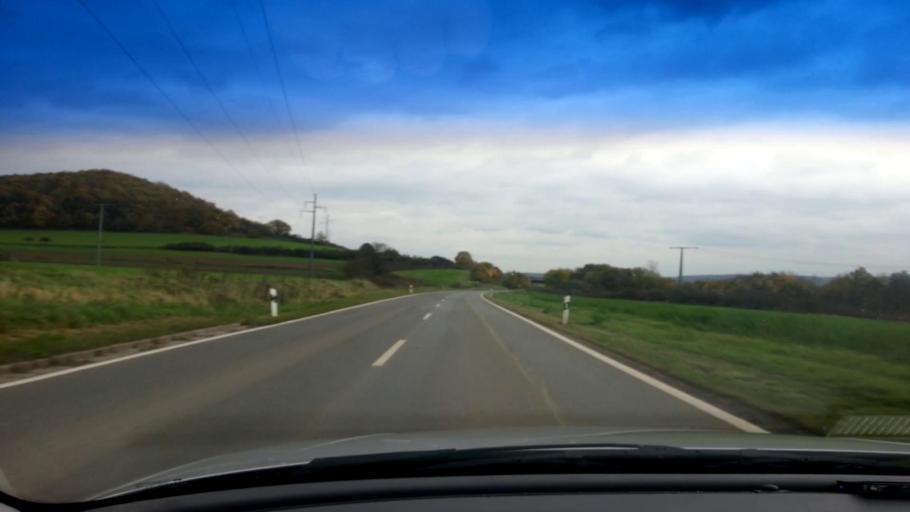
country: DE
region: Bavaria
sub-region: Regierungsbezirk Unterfranken
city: Stettfeld
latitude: 49.9644
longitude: 10.7286
